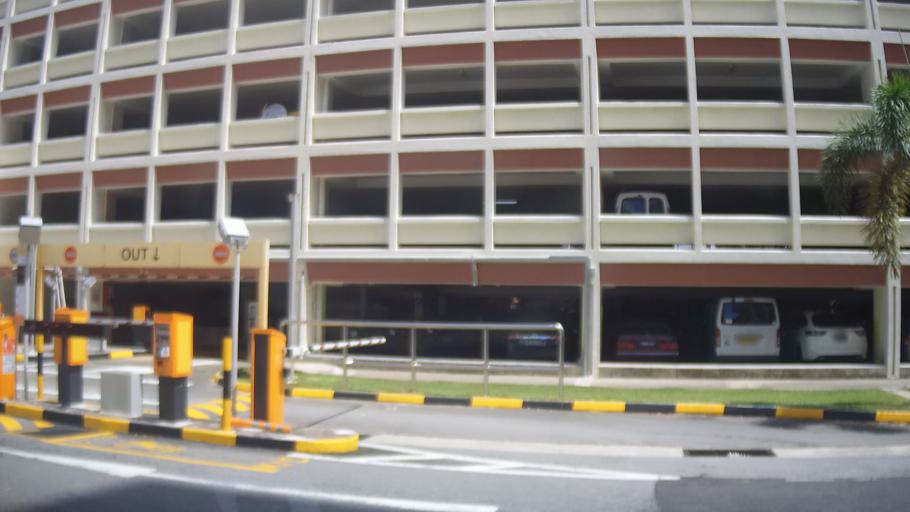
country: SG
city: Singapore
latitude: 1.3242
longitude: 103.8864
